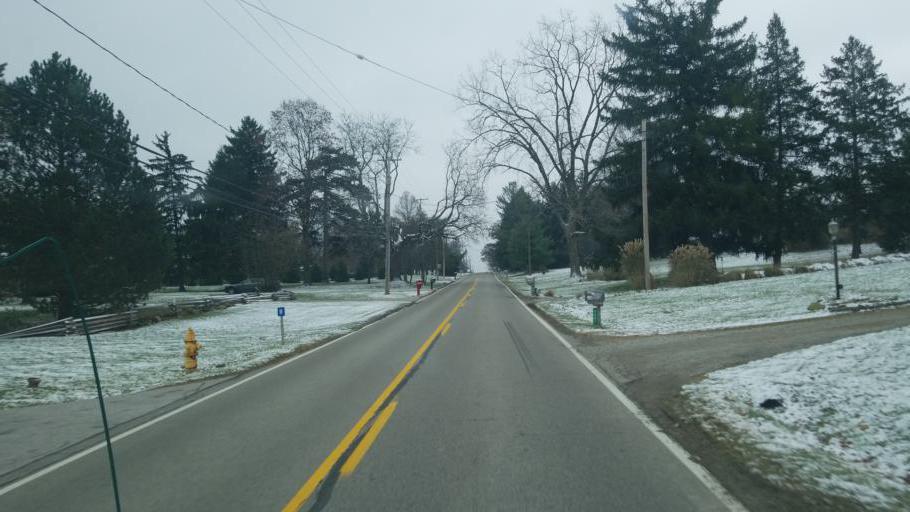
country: US
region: Ohio
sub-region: Cuyahoga County
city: North Royalton
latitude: 41.2807
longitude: -81.7162
